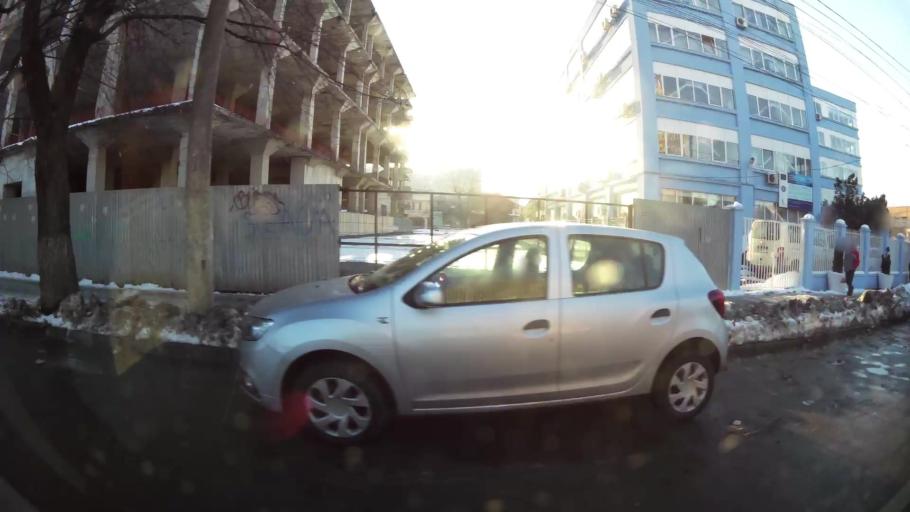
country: RO
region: Bucuresti
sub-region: Municipiul Bucuresti
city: Bucharest
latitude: 44.4480
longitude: 26.1321
